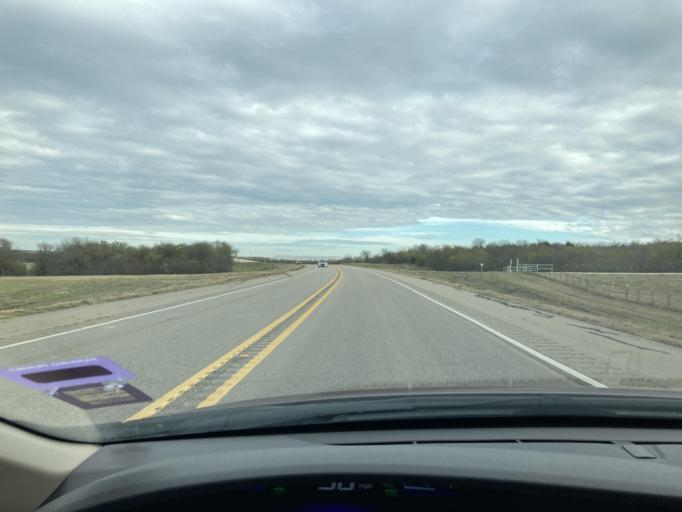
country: US
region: Texas
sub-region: Navarro County
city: Corsicana
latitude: 32.0418
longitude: -96.4612
